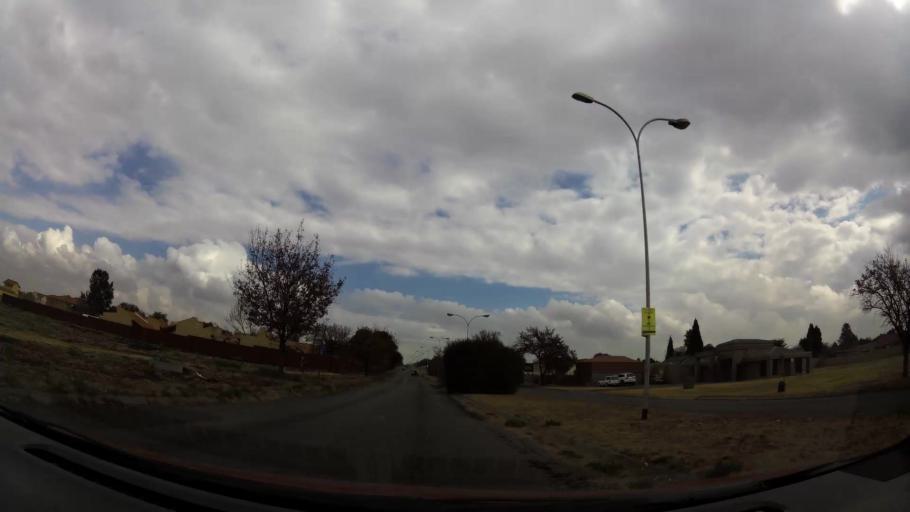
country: ZA
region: Gauteng
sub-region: Sedibeng District Municipality
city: Vanderbijlpark
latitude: -26.7298
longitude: 27.8590
